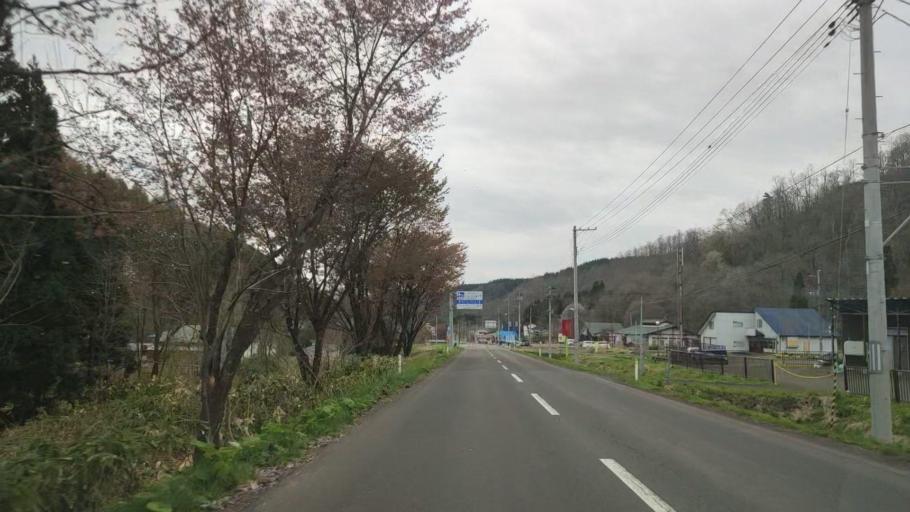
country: JP
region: Akita
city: Hanawa
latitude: 40.3579
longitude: 140.7843
